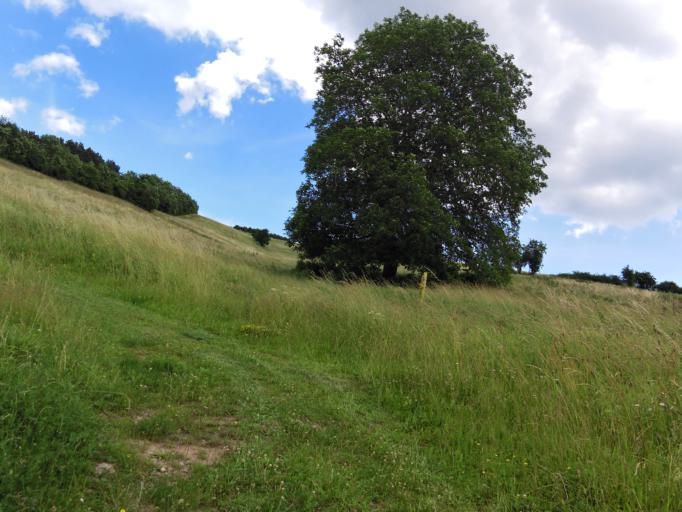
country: DE
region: Thuringia
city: Lauchroden
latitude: 50.9906
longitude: 10.1611
